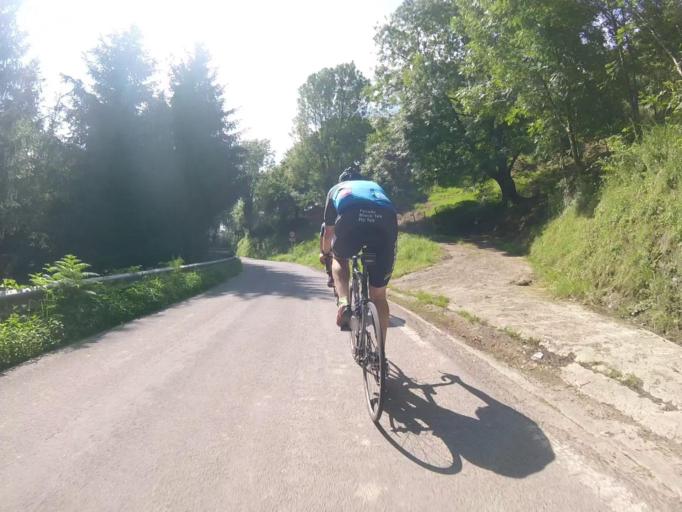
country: ES
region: Basque Country
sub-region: Provincia de Guipuzcoa
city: Orendain
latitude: 43.0775
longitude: -2.1072
